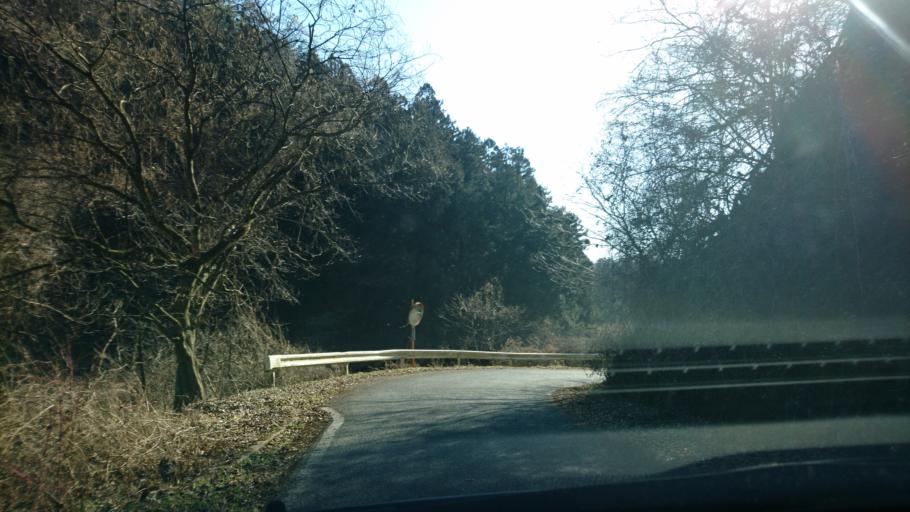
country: JP
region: Iwate
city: Ichinoseki
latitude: 38.7991
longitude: 141.2592
